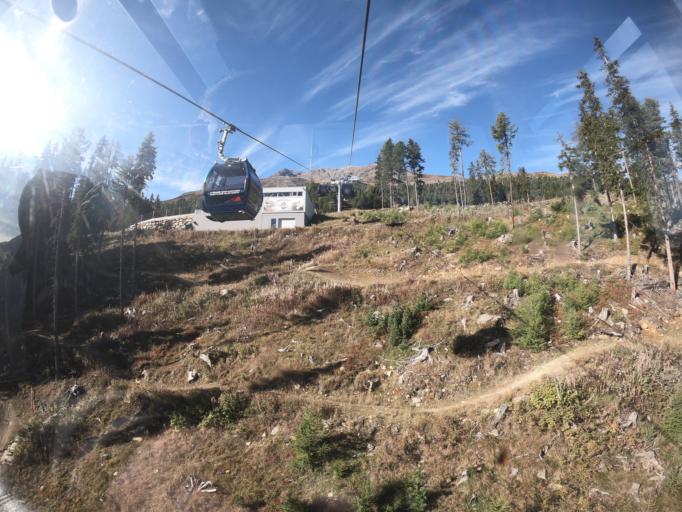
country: AT
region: Tyrol
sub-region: Politischer Bezirk Imst
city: Soelden
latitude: 46.9551
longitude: 10.9979
